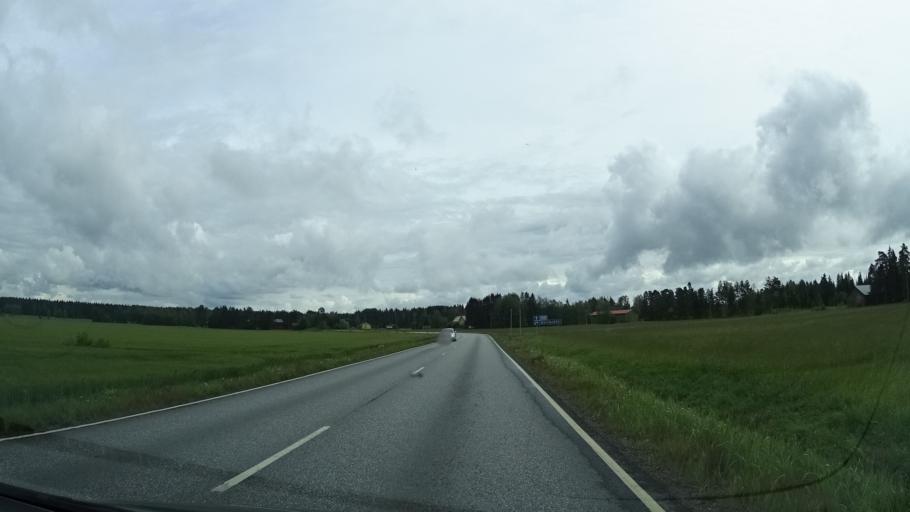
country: FI
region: Haeme
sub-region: Forssa
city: Humppila
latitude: 61.0983
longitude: 23.3095
